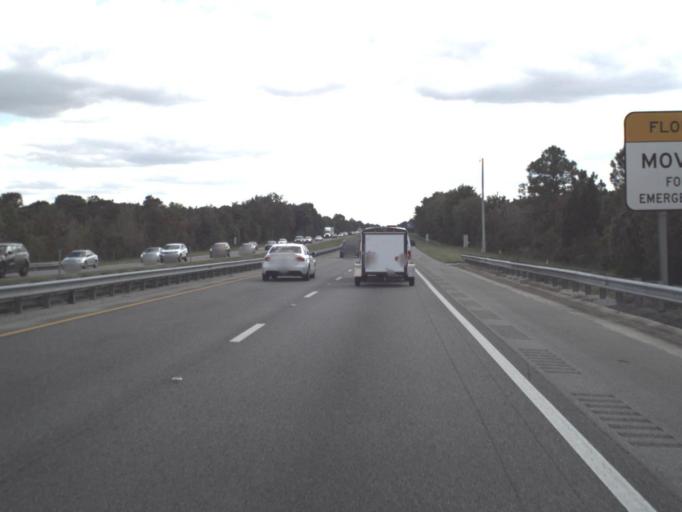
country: US
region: Florida
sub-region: Osceola County
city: Saint Cloud
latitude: 28.1488
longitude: -81.2964
